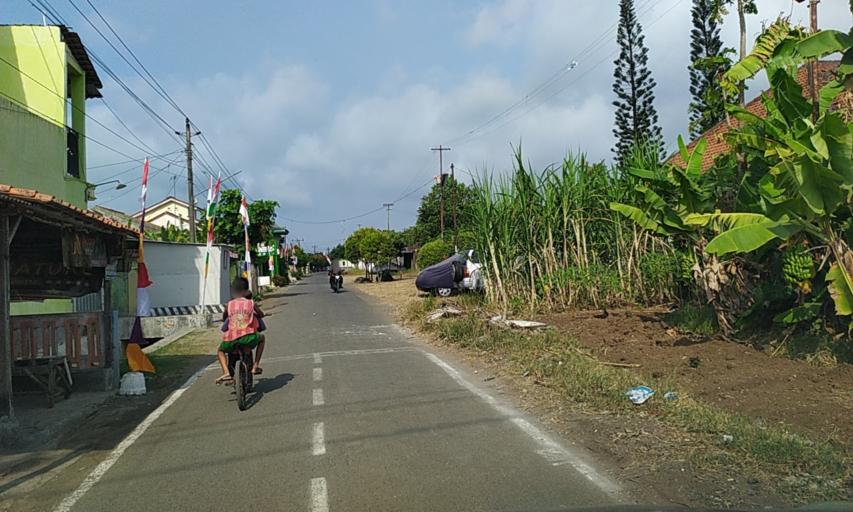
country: ID
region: Central Java
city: Karangbadar Kidul
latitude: -7.7371
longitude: 109.0010
